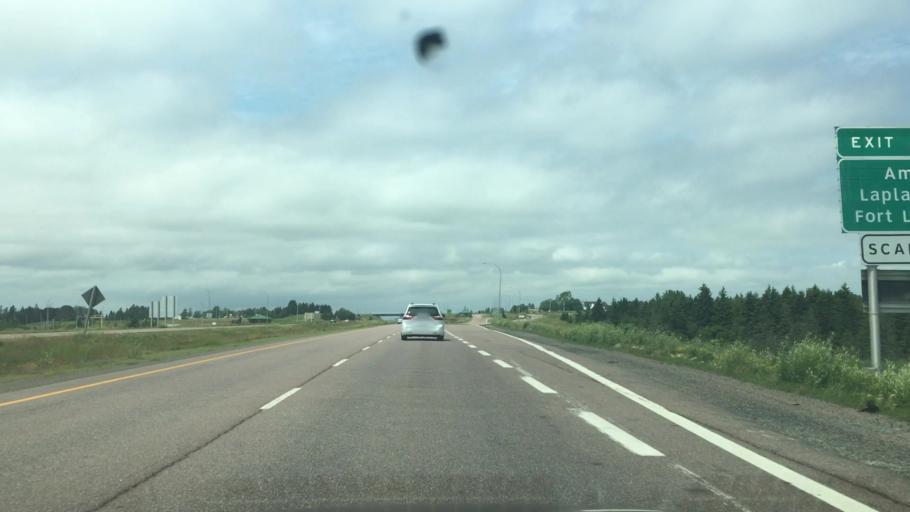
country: CA
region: Nova Scotia
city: Amherst
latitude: 45.8490
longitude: -64.2460
